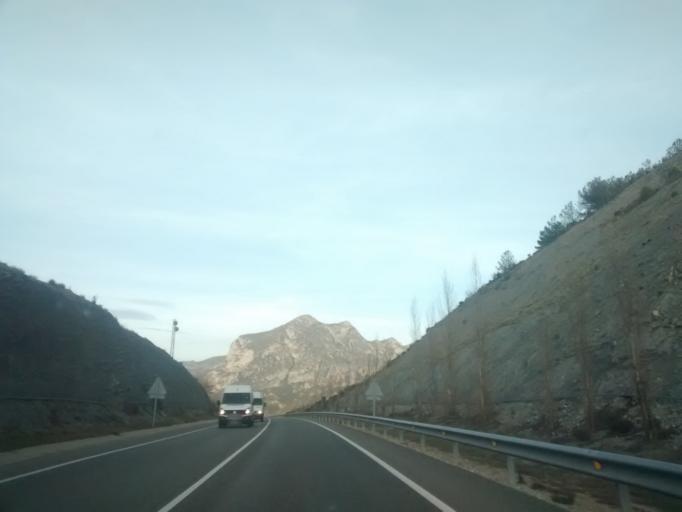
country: ES
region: Catalonia
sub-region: Provincia de Lleida
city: Coll de Nargo
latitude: 42.1540
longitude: 1.3097
